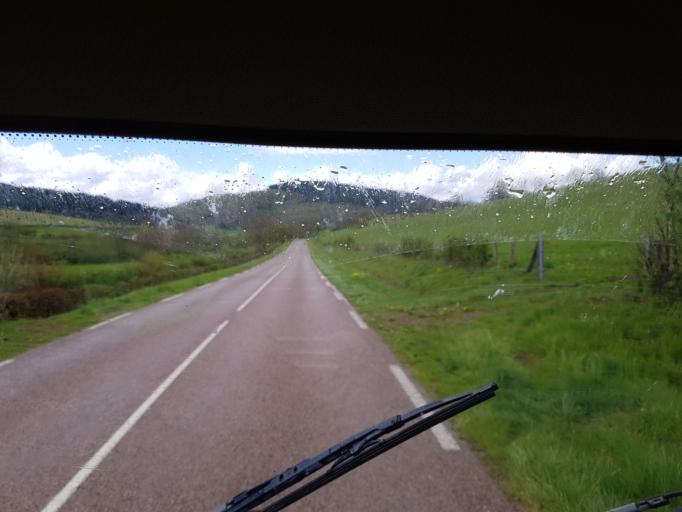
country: FR
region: Bourgogne
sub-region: Departement de Saone-et-Loire
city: Autun
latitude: 47.0612
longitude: 4.2592
